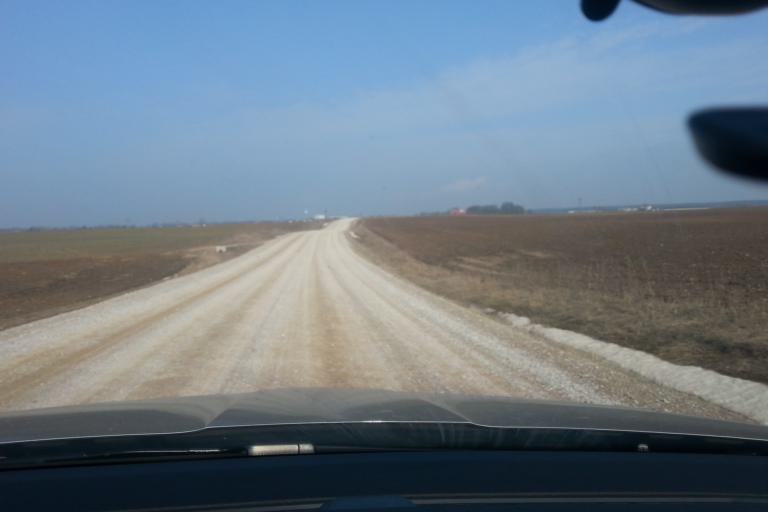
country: LT
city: Trakai
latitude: 54.5951
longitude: 24.9777
